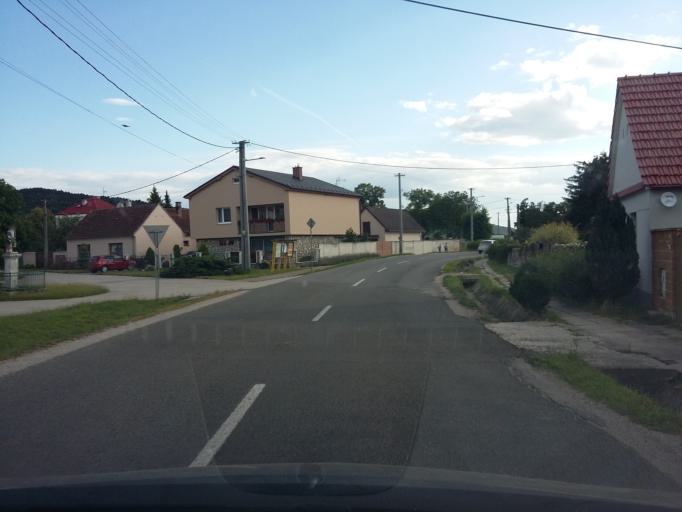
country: SK
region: Trnavsky
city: Smolenice
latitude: 48.5347
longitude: 17.3238
